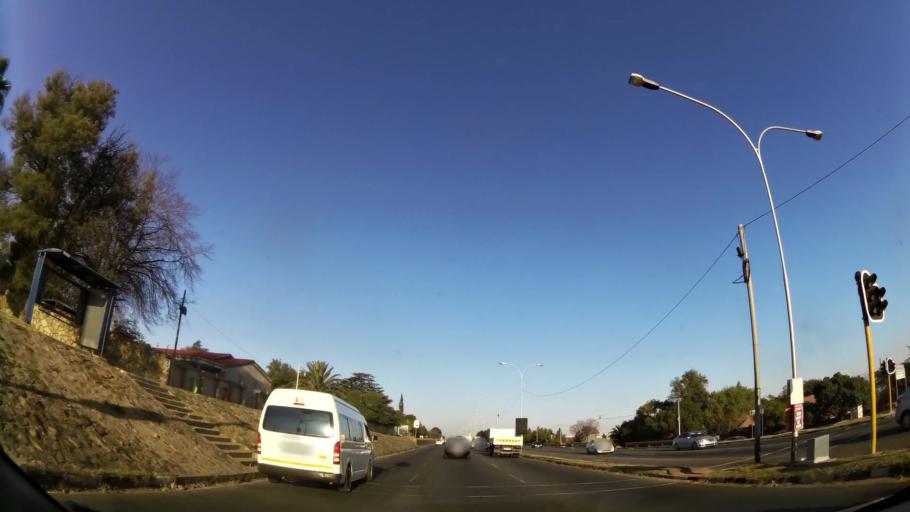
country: ZA
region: Gauteng
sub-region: City of Johannesburg Metropolitan Municipality
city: Roodepoort
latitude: -26.1512
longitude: 27.9070
